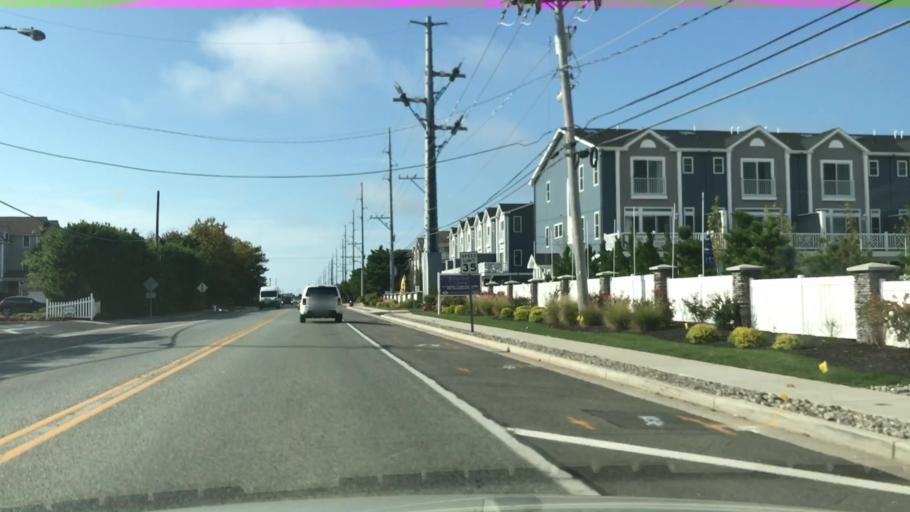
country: US
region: New Jersey
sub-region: Cape May County
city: Cape May Court House
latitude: 39.0583
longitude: -74.7675
